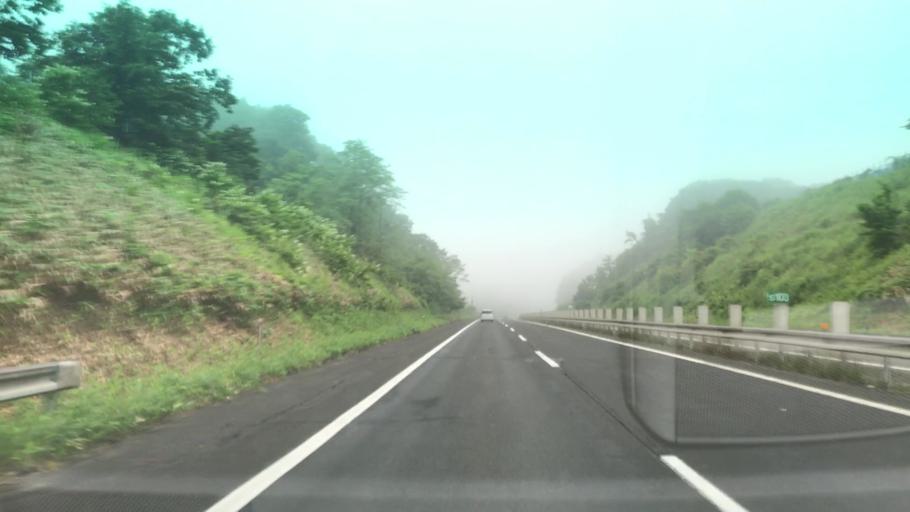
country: JP
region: Hokkaido
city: Muroran
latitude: 42.4398
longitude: 141.1393
